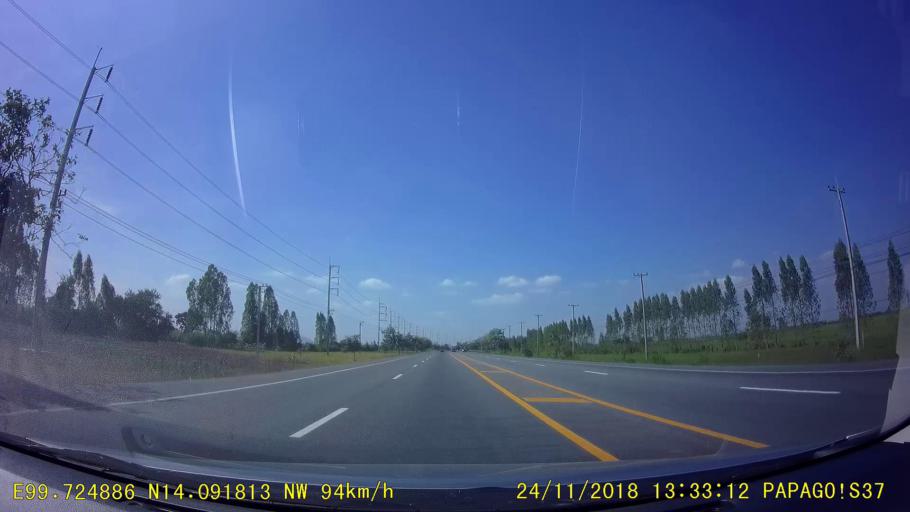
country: TH
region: Kanchanaburi
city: Phanom Thuan
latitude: 14.0922
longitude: 99.7242
